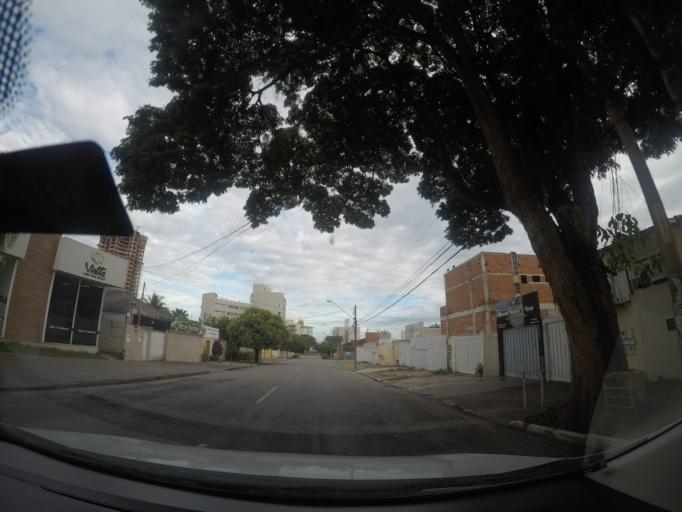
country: BR
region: Goias
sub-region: Goiania
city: Goiania
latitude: -16.6856
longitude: -49.2755
